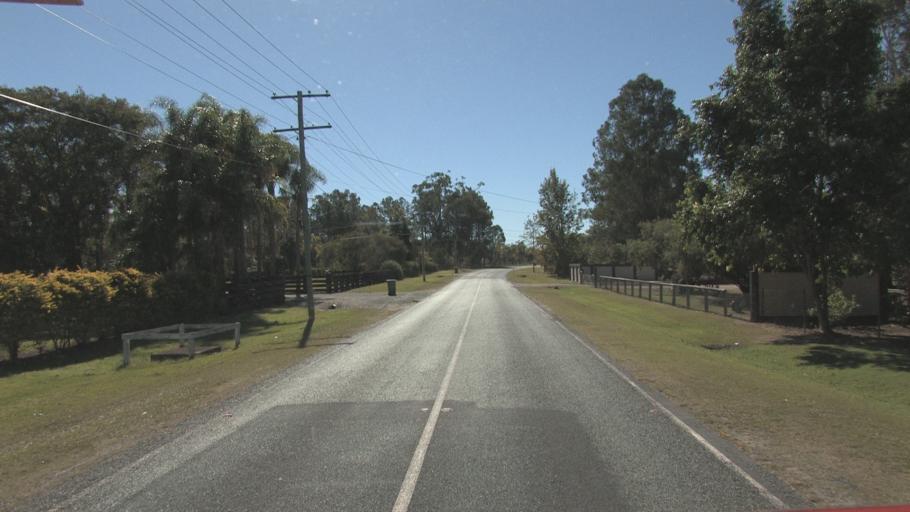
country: AU
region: Queensland
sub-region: Logan
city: Park Ridge South
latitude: -27.7263
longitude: 153.0531
